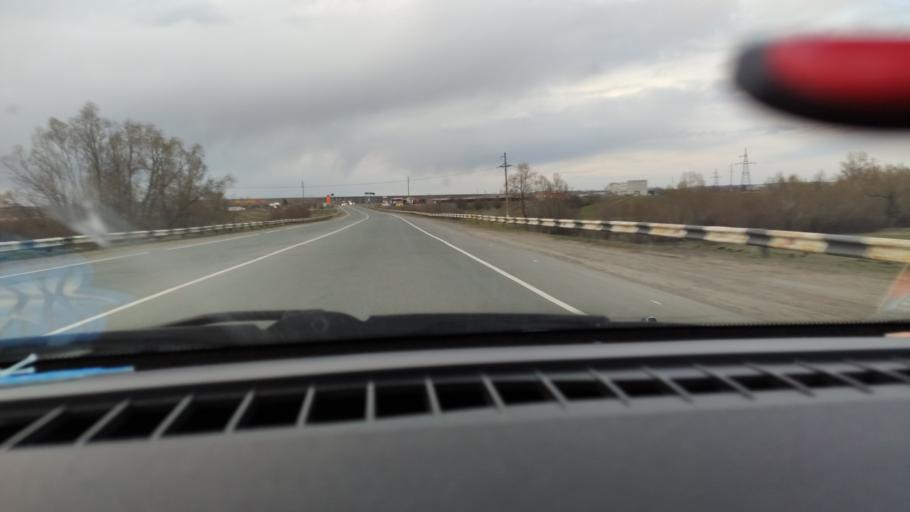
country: RU
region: Saratov
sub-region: Saratovskiy Rayon
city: Saratov
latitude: 51.7319
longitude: 46.0339
